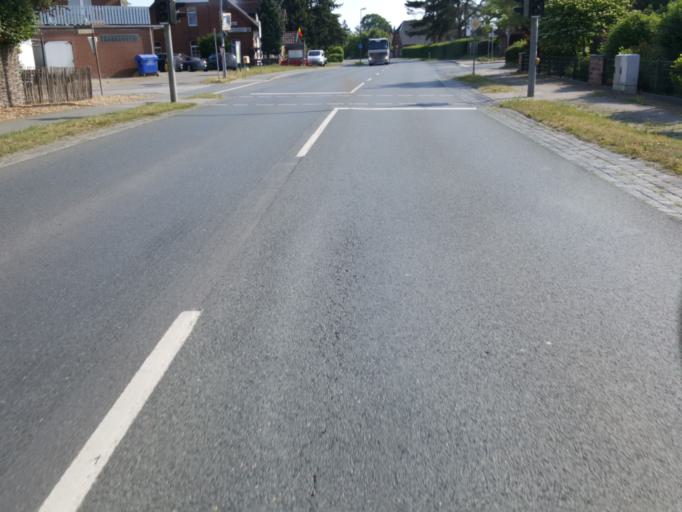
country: DE
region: Lower Saxony
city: Estorf
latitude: 52.5967
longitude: 9.1525
